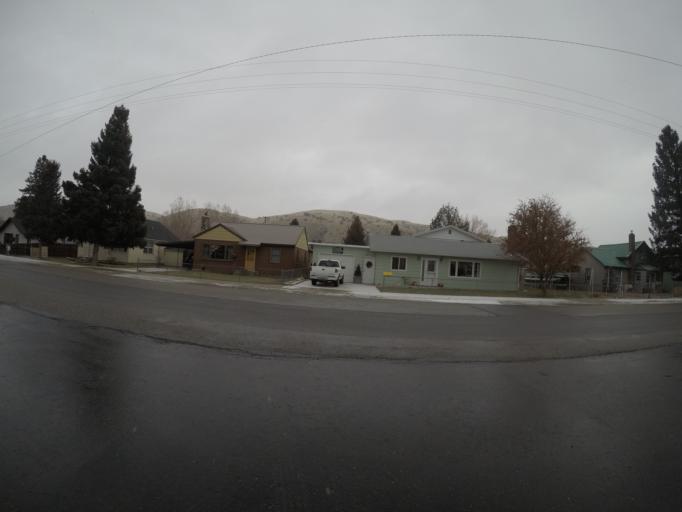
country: US
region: Montana
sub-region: Stillwater County
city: Absarokee
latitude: 45.5173
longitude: -109.4440
